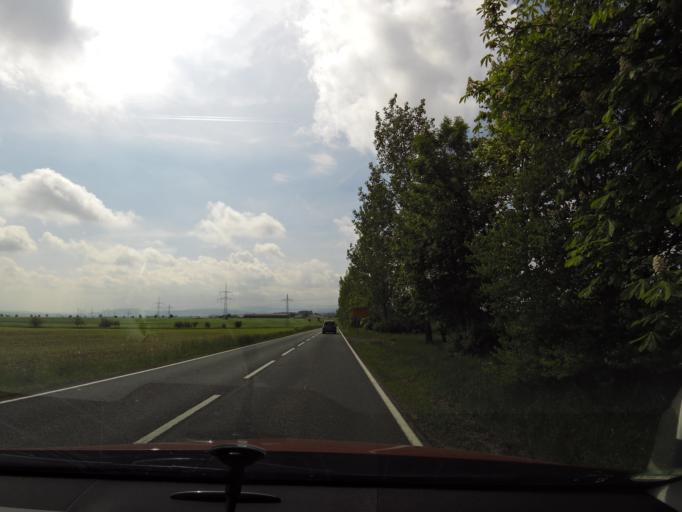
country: DE
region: Thuringia
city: Lauterbach
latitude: 51.0338
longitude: 10.3320
